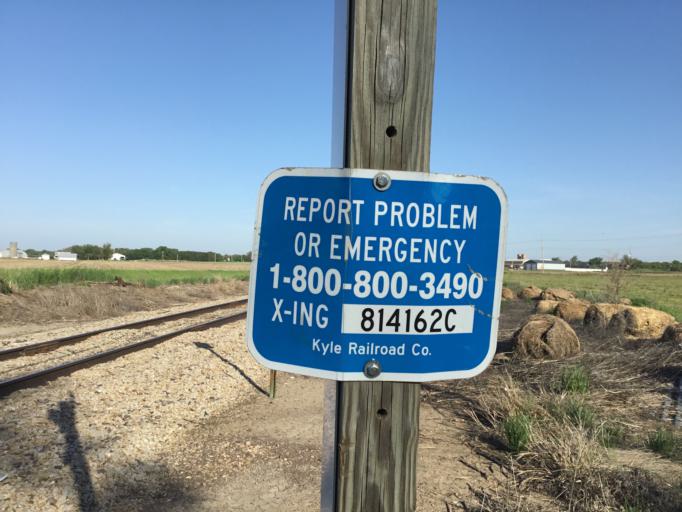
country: US
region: Kansas
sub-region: Mitchell County
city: Beloit
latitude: 39.4500
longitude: -98.0880
